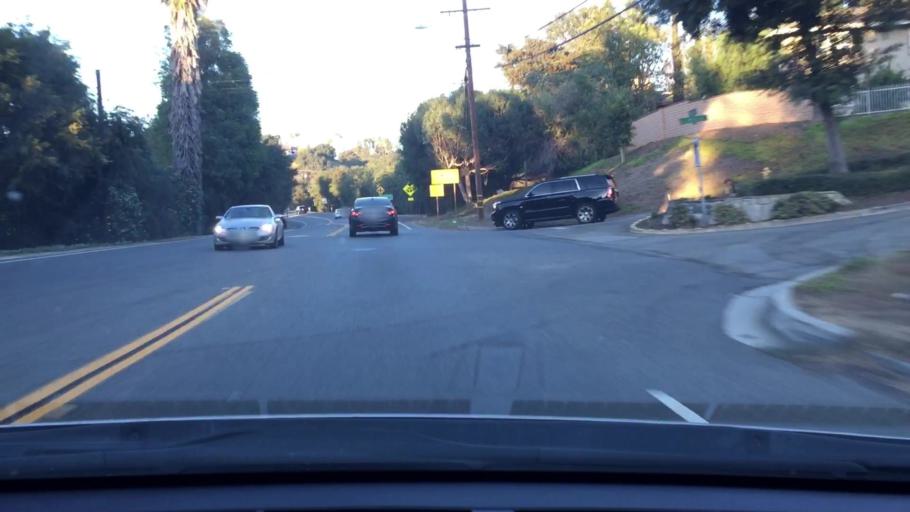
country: US
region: California
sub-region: San Bernardino County
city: Chino Hills
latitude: 33.9603
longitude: -117.7656
